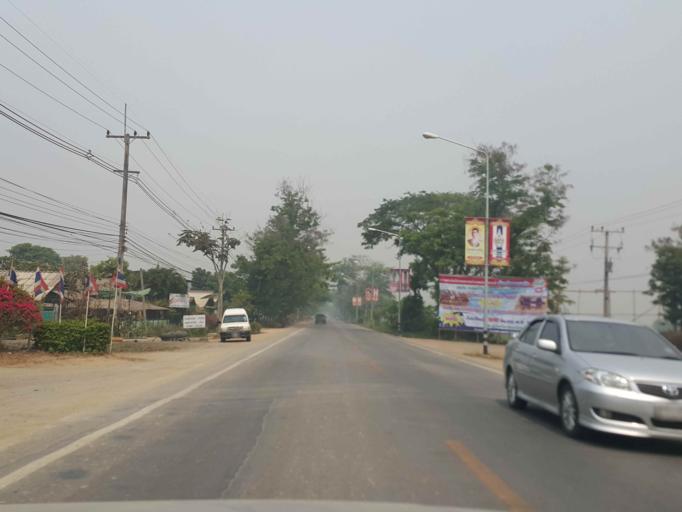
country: TH
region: Chiang Mai
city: Mae Taeng
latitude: 19.0143
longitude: 98.9709
